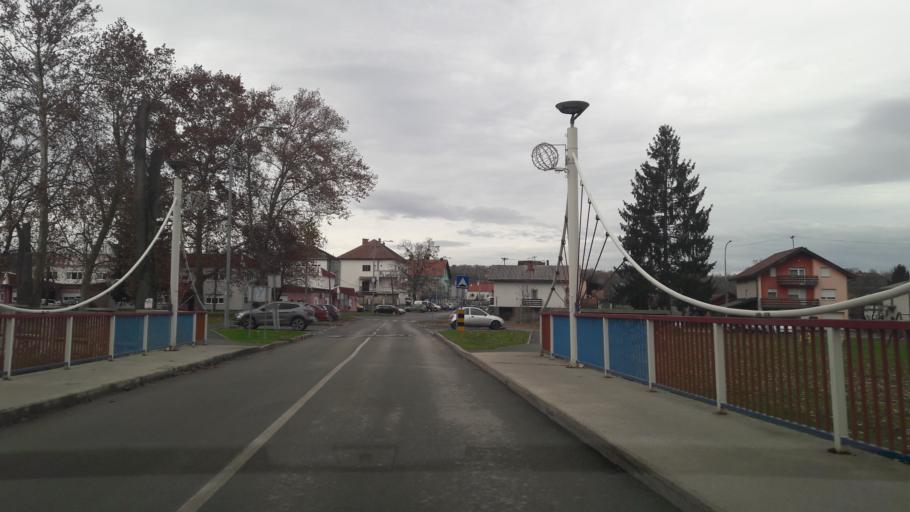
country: HR
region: Virovitick-Podravska
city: Orahovica
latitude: 45.5316
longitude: 17.8824
